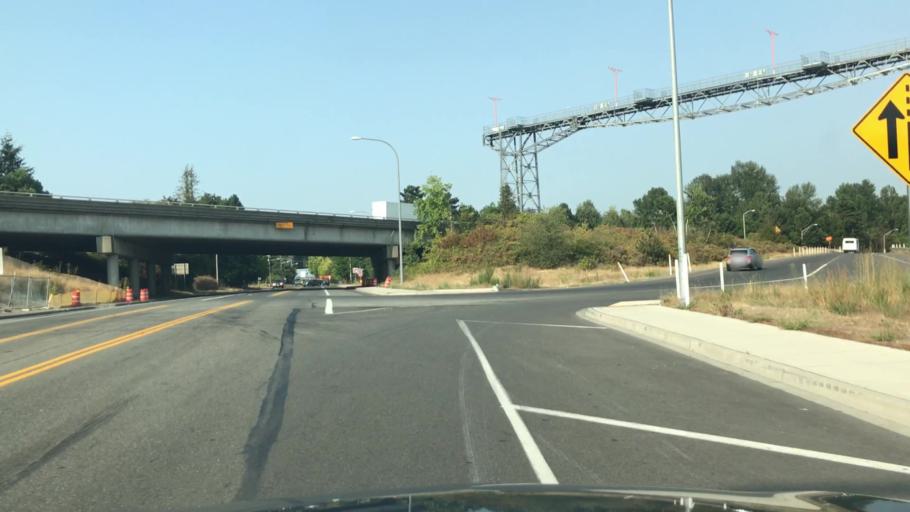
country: US
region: Washington
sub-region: King County
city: Boulevard Park
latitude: 47.4693
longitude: -122.3197
